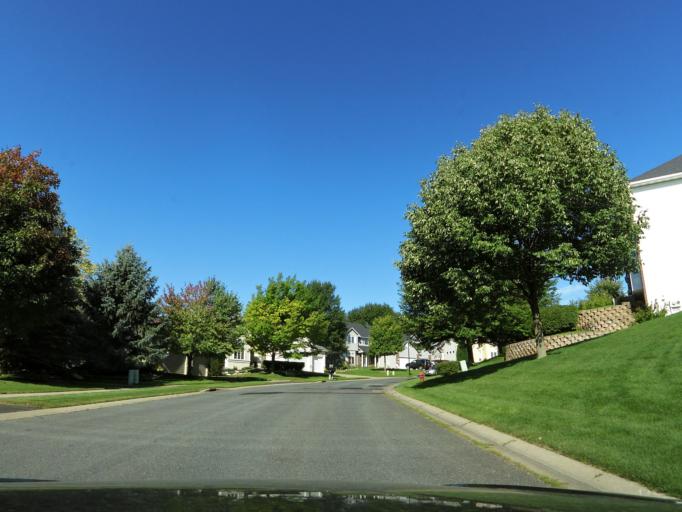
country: US
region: Minnesota
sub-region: Scott County
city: Savage
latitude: 44.7318
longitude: -93.3484
